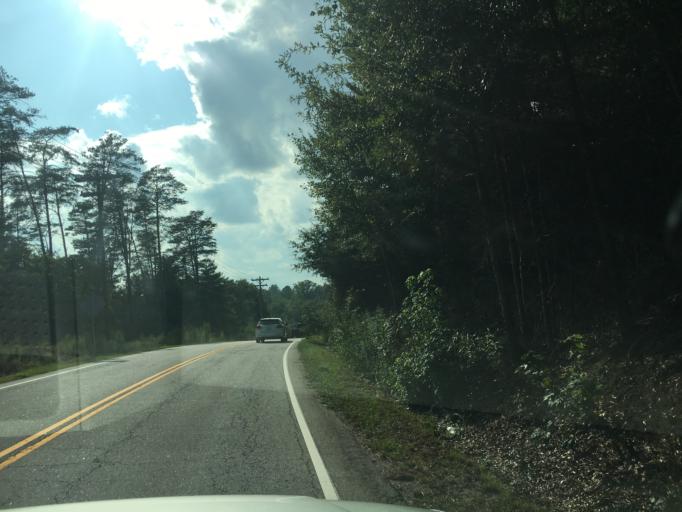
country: US
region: South Carolina
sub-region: Greenville County
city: Taylors
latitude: 34.9446
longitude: -82.3185
